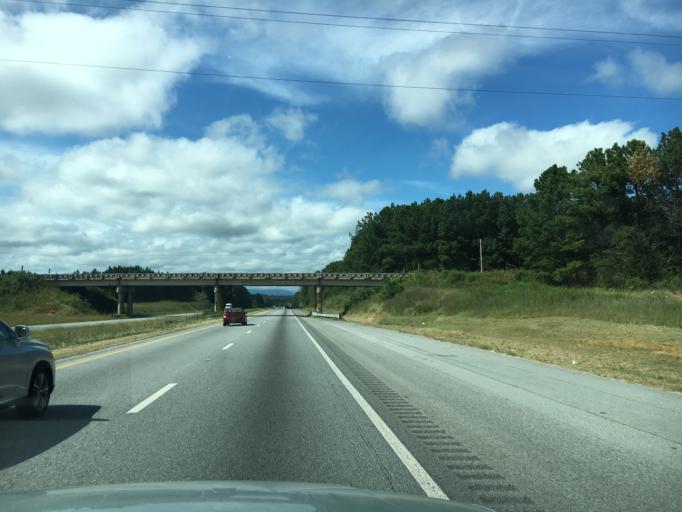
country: US
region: South Carolina
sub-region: Spartanburg County
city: Inman
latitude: 35.0892
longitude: -82.0694
